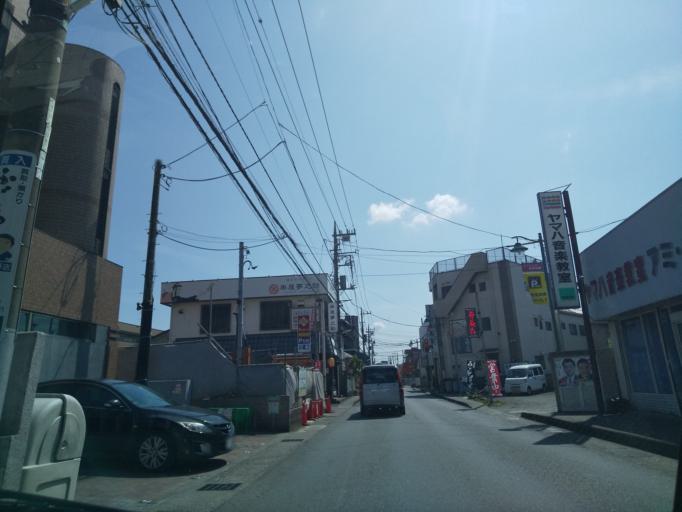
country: JP
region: Kanagawa
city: Minami-rinkan
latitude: 35.4726
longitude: 139.4276
